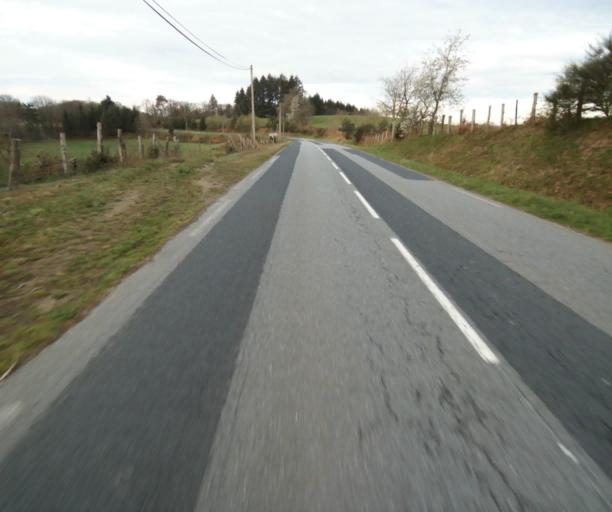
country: FR
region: Limousin
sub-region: Departement de la Correze
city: Correze
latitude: 45.3841
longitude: 1.8656
